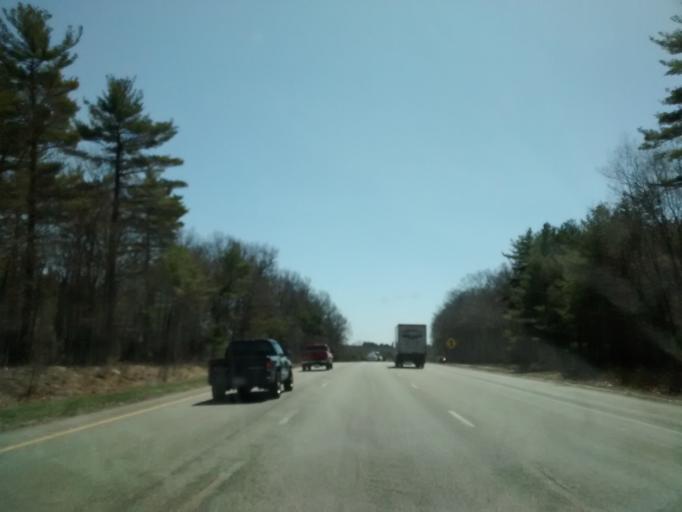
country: US
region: Massachusetts
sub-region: Middlesex County
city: Hopkinton
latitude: 42.2115
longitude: -71.5450
